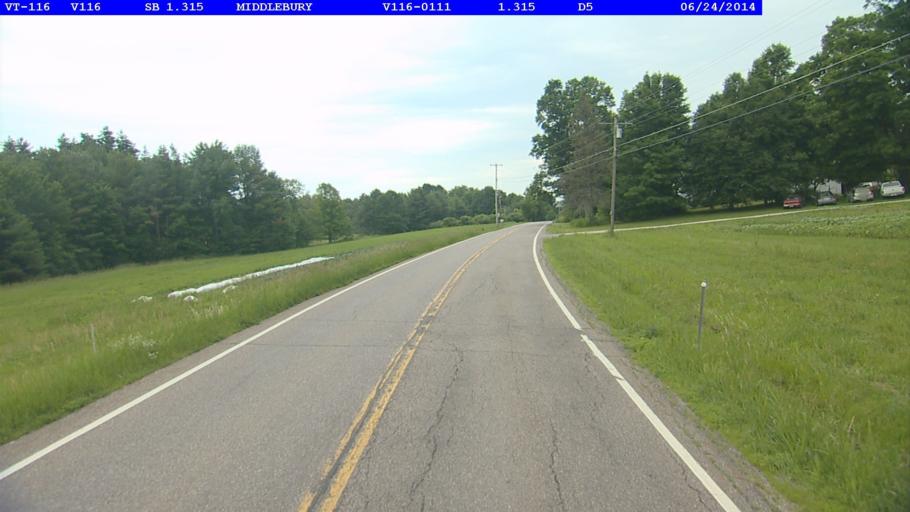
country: US
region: Vermont
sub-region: Addison County
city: Middlebury (village)
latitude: 43.9836
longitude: -73.1039
